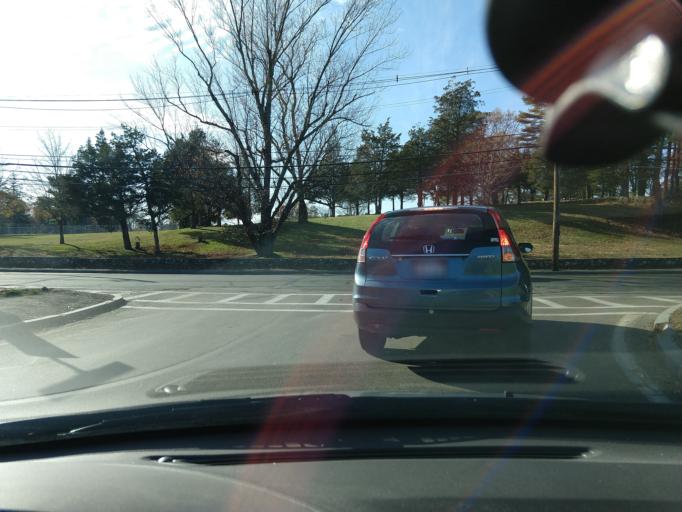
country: US
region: Massachusetts
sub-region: Middlesex County
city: Burlington
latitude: 42.5064
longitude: -71.1955
